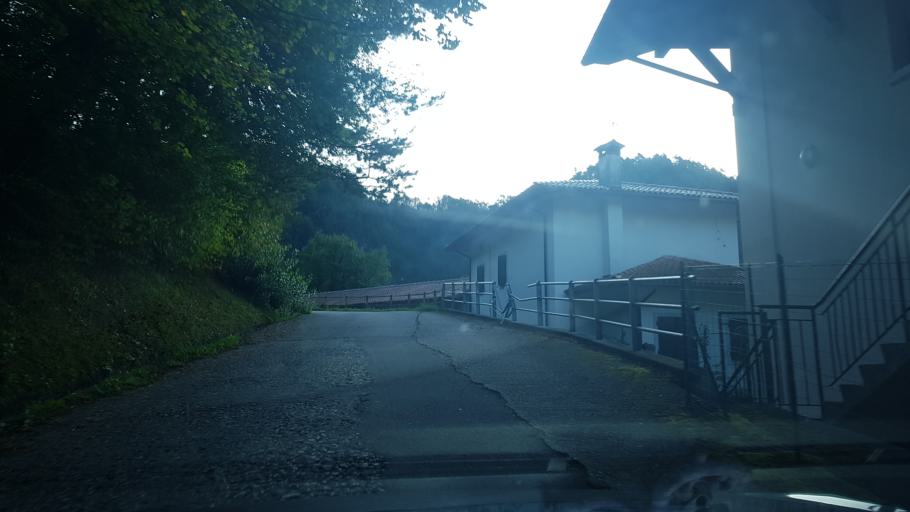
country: IT
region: Friuli Venezia Giulia
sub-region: Provincia di Pordenone
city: Frisanco
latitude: 46.2556
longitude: 12.7373
